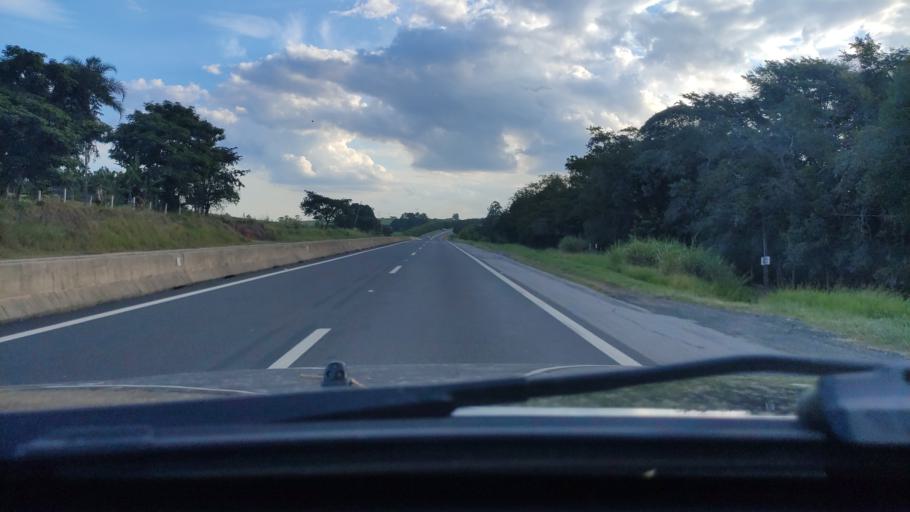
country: BR
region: Sao Paulo
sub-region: Mogi-Mirim
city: Mogi Mirim
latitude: -22.4441
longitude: -47.0534
